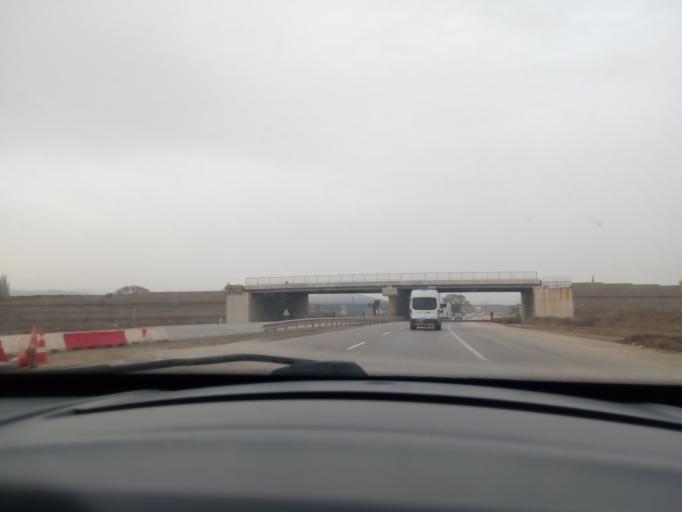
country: TR
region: Bursa
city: Tatkavakli
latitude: 40.0342
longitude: 28.3732
